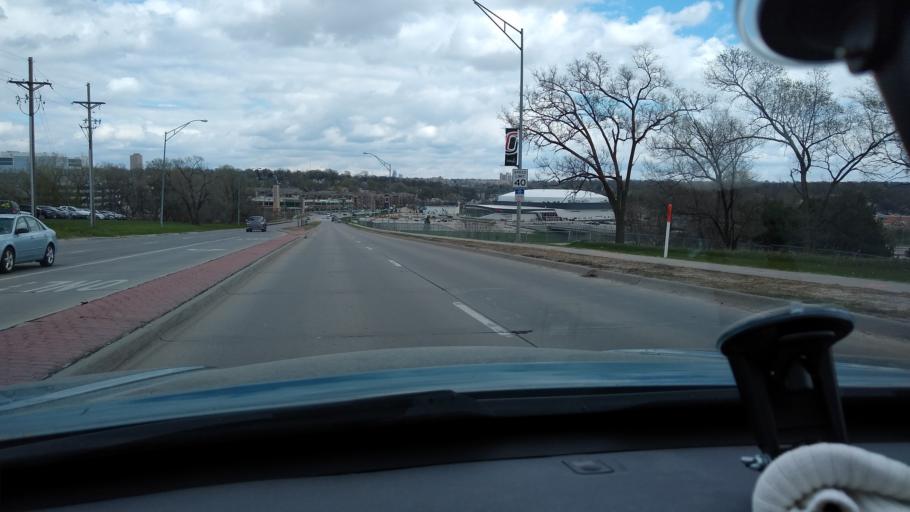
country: US
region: Nebraska
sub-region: Douglas County
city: Ralston
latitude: 41.2353
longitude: -96.0209
